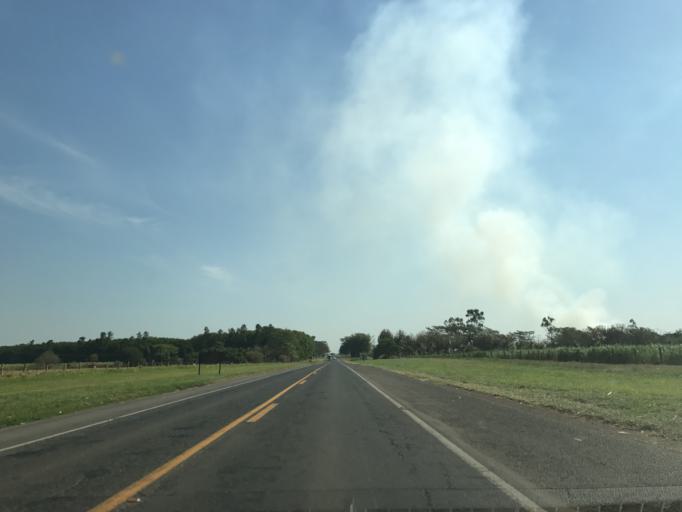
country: BR
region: Sao Paulo
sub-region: Penapolis
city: Penapolis
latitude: -21.3890
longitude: -50.0989
